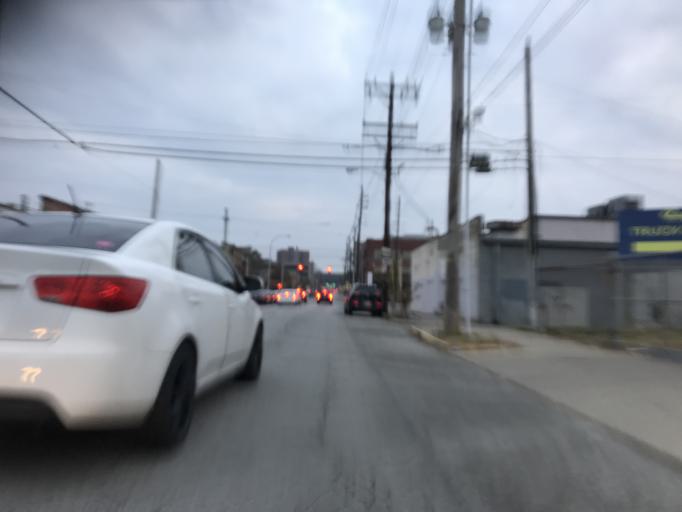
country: US
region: Kentucky
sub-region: Jefferson County
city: Louisville
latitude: 38.2443
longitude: -85.7457
